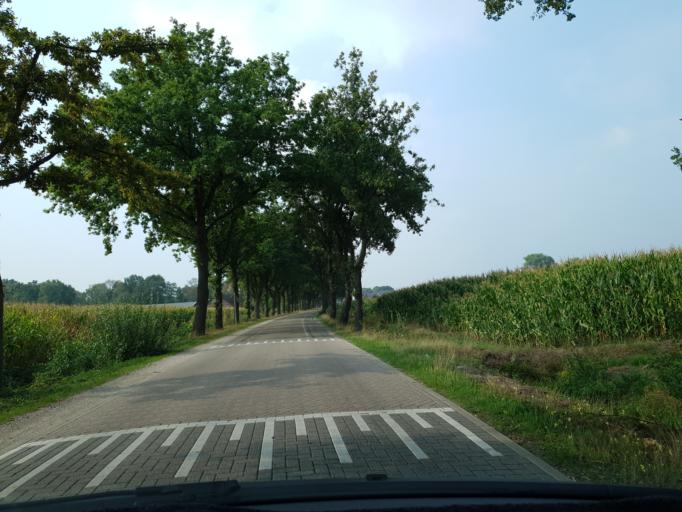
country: NL
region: North Brabant
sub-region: Gemeente Valkenswaard
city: Valkenswaard
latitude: 51.3401
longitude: 5.4360
